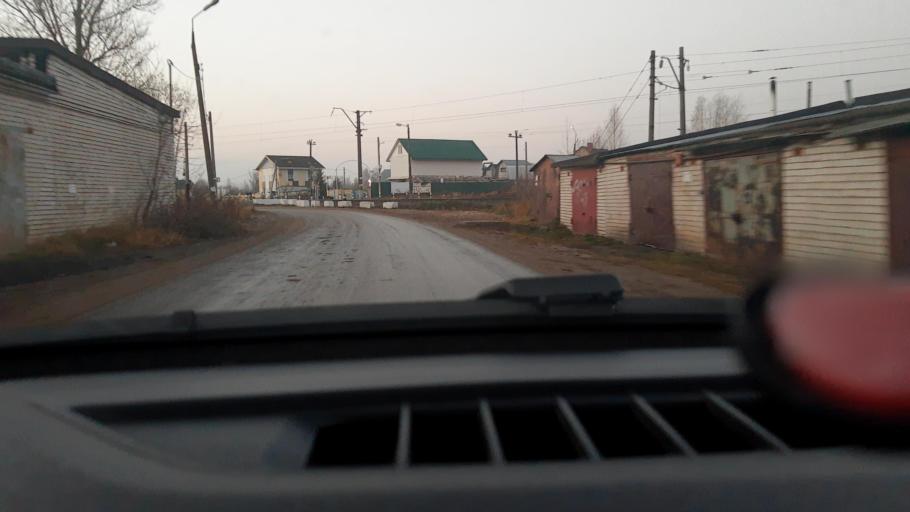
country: RU
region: Nizjnij Novgorod
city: Gorbatovka
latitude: 56.3261
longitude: 43.8383
